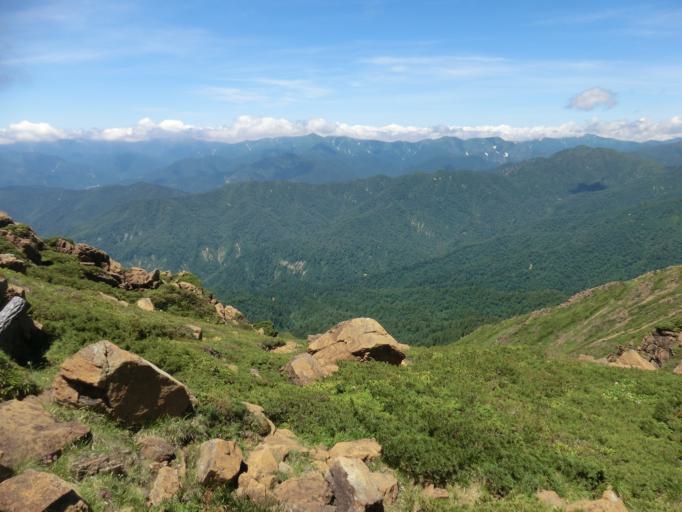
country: JP
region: Gunma
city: Numata
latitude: 36.9021
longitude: 139.1721
